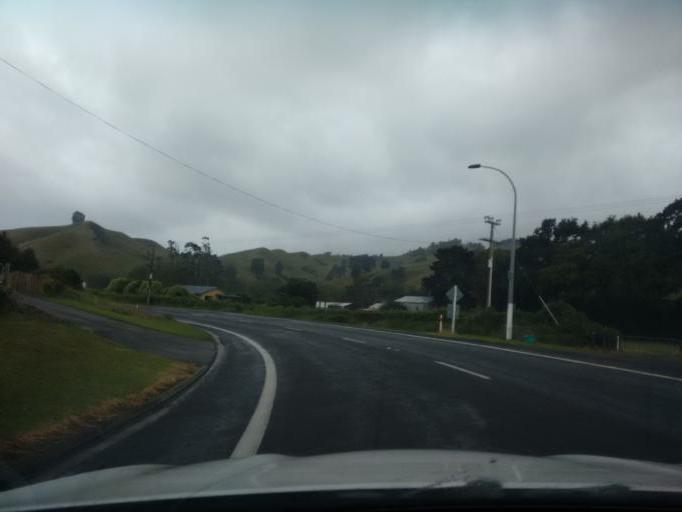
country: NZ
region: Waikato
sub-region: Thames-Coromandel District
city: Whitianga
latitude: -36.7930
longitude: 175.7251
